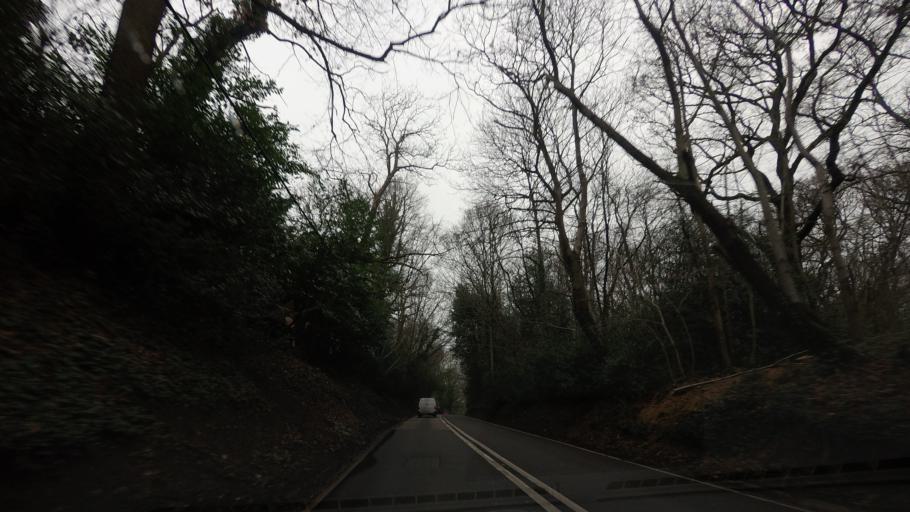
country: GB
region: England
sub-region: East Sussex
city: Battle
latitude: 50.9186
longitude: 0.5369
